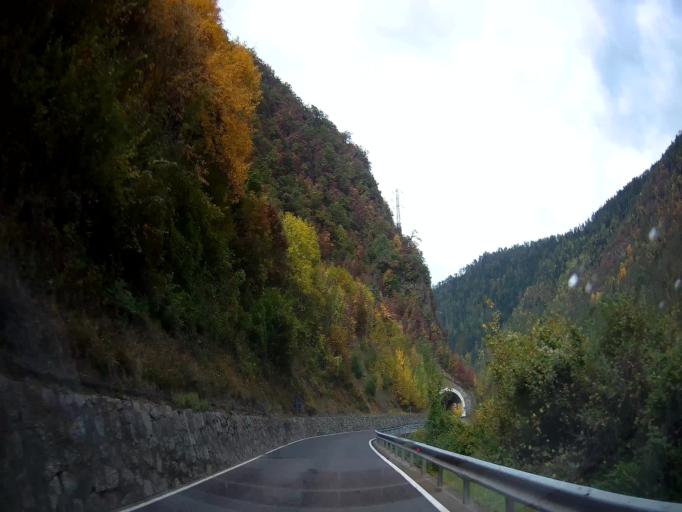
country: IT
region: Trentino-Alto Adige
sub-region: Bolzano
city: Naturno
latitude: 46.6622
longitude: 10.9536
